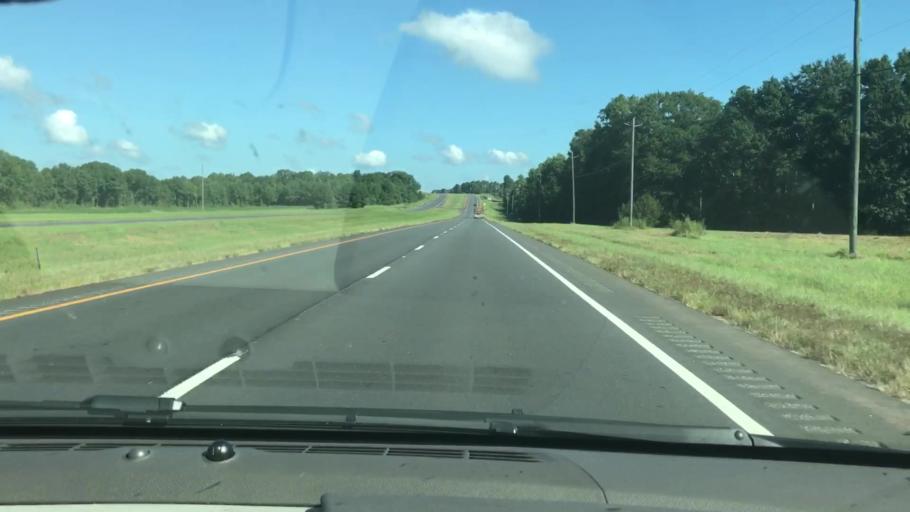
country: US
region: Alabama
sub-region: Barbour County
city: Eufaula
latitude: 32.0207
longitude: -85.1180
